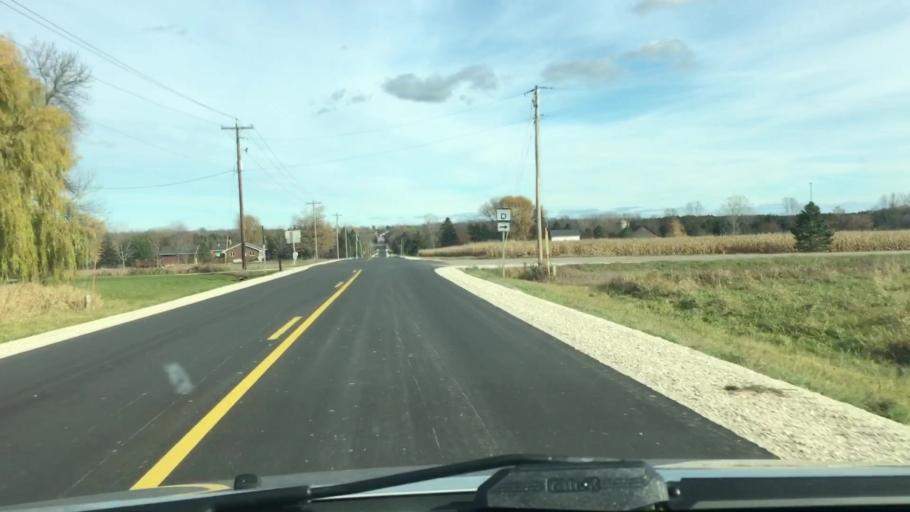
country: US
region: Wisconsin
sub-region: Kewaunee County
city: Algoma
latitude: 44.6901
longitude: -87.5003
